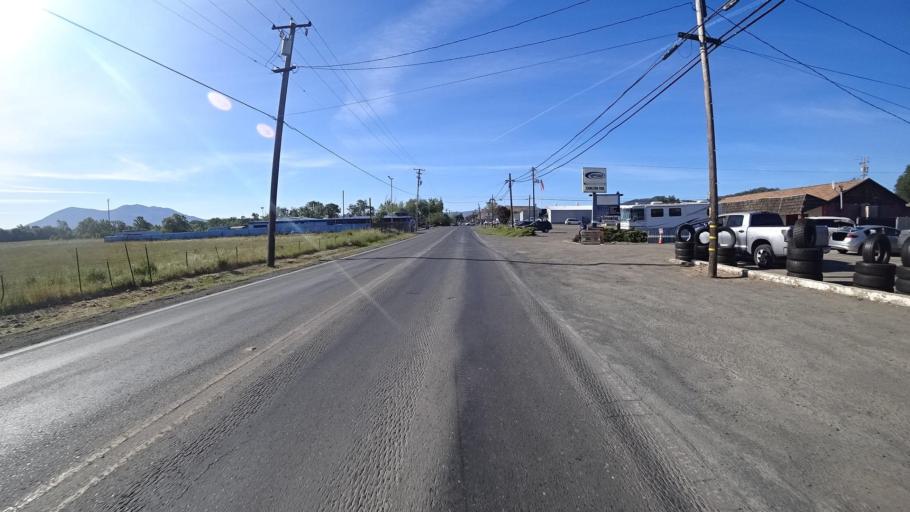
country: US
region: California
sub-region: Lake County
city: Lakeport
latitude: 39.0230
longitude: -122.9147
